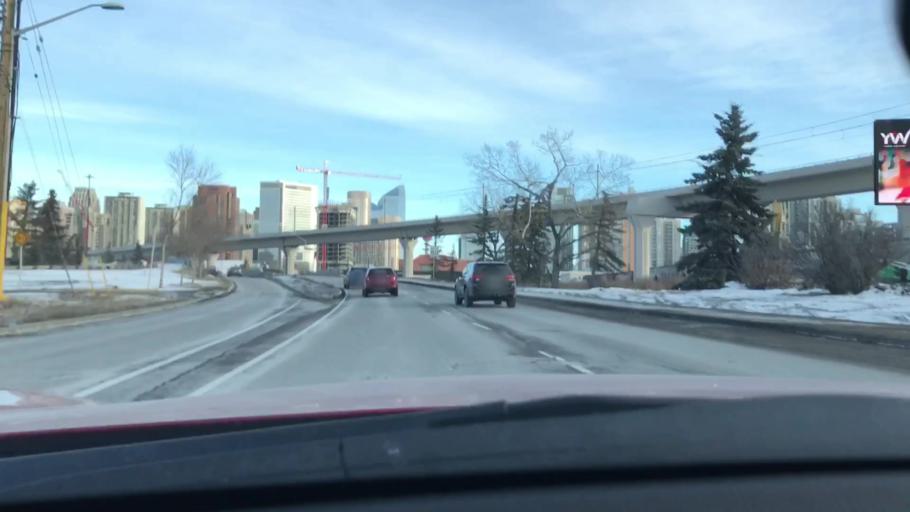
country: CA
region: Alberta
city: Calgary
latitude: 51.0453
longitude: -114.0966
